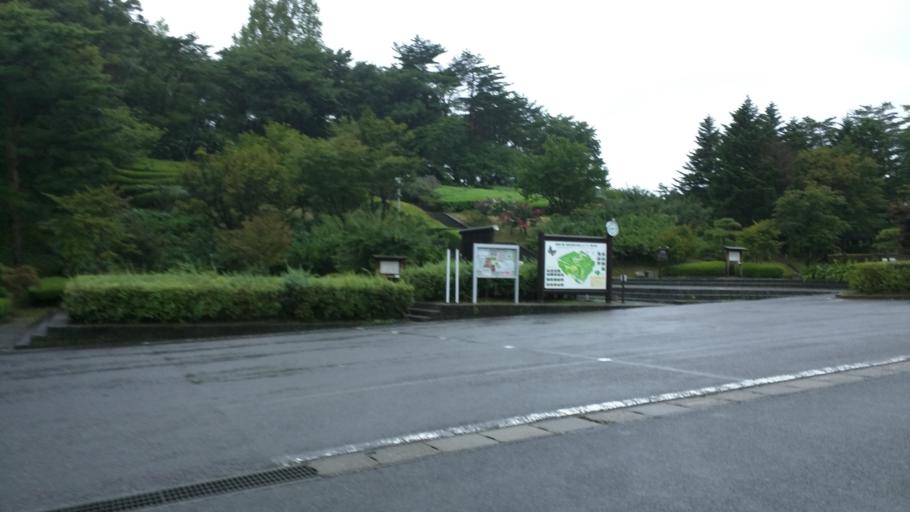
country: JP
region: Fukushima
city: Koriyama
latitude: 37.4149
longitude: 140.2734
